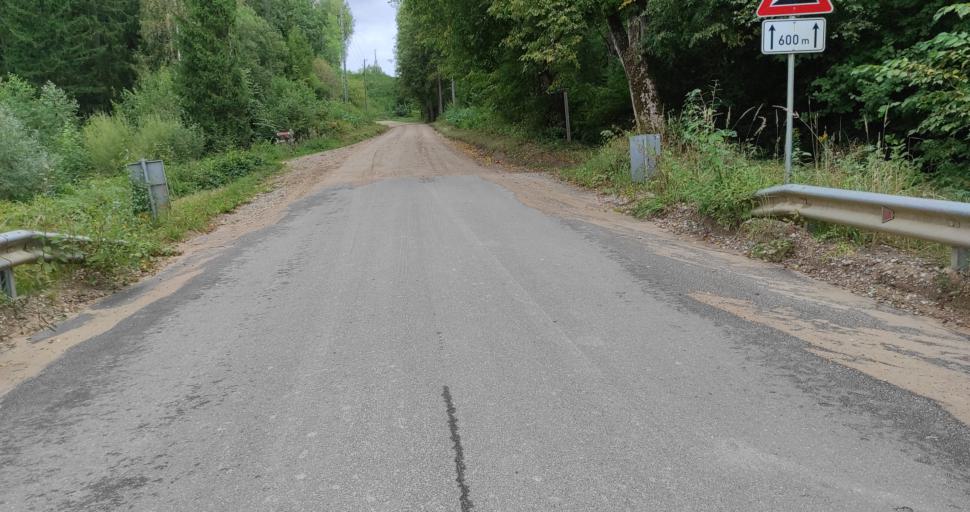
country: LV
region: Amatas Novads
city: Drabesi
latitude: 57.2374
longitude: 25.2012
